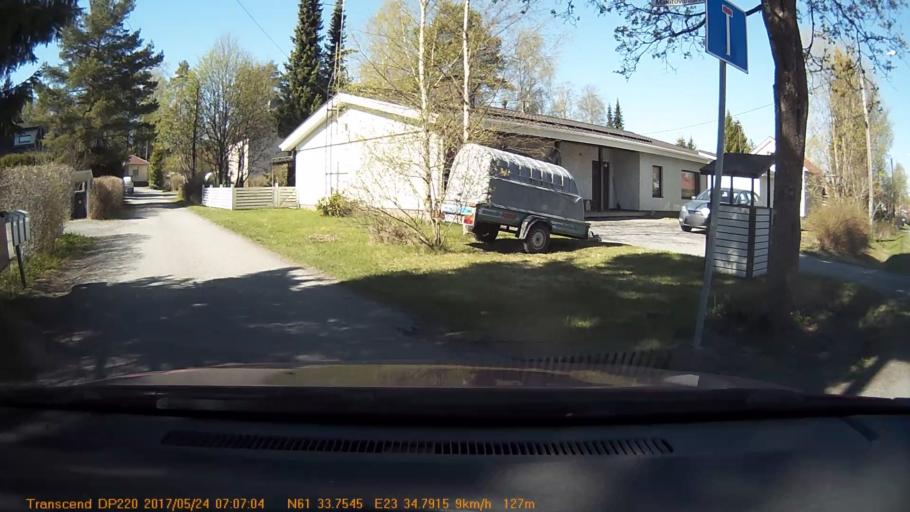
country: FI
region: Pirkanmaa
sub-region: Tampere
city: Yloejaervi
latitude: 61.5626
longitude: 23.5799
